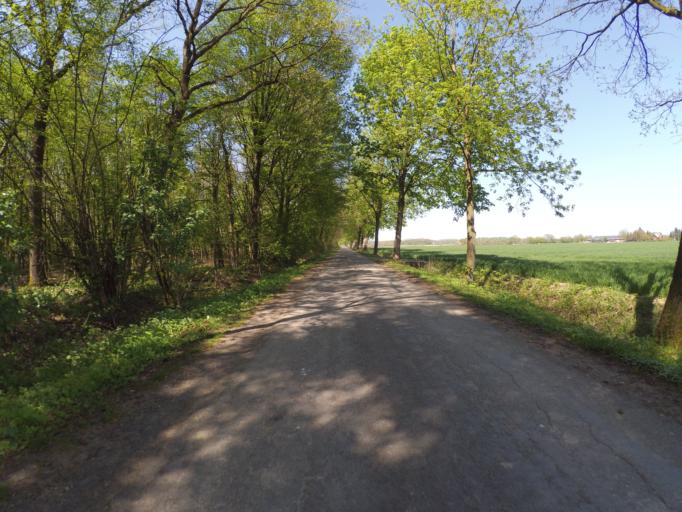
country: DE
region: North Rhine-Westphalia
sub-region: Regierungsbezirk Munster
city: Ascheberg
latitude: 51.8003
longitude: 7.6046
